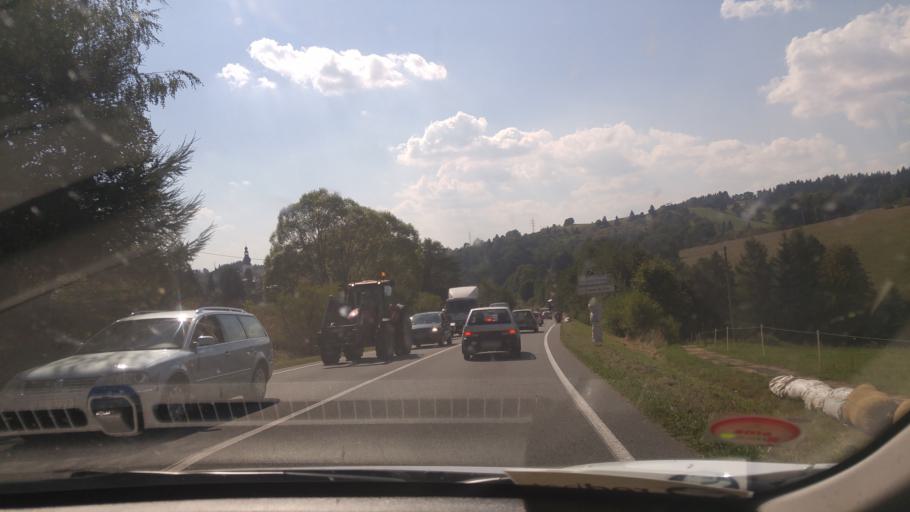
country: CZ
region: Olomoucky
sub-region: Okres Sumperk
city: Stare Mesto
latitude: 50.1576
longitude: 17.0148
